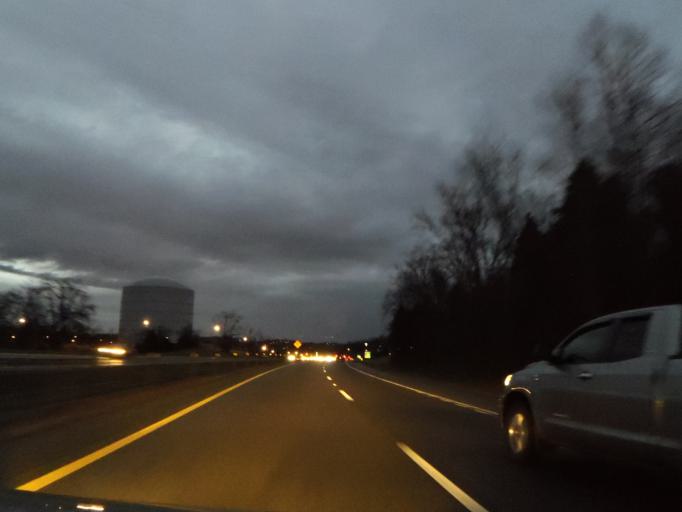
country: US
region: Tennessee
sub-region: Sullivan County
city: Colonial Heights
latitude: 36.4394
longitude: -82.5233
